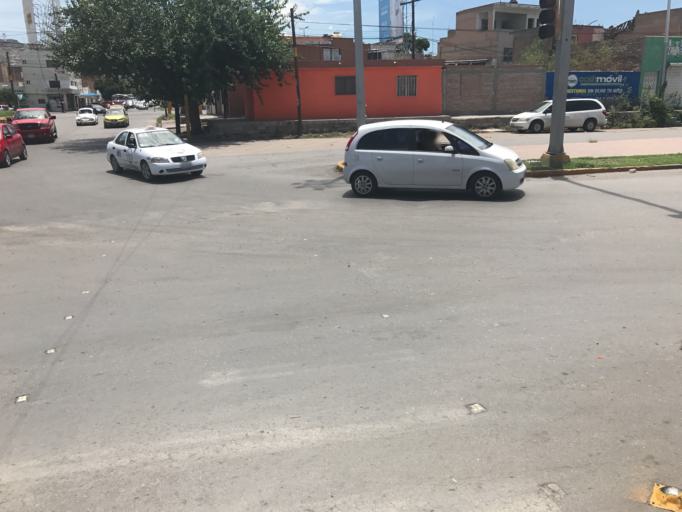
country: MX
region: Durango
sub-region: Lerdo
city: El Huarache (El Guarache)
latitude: 25.5432
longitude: -103.4601
